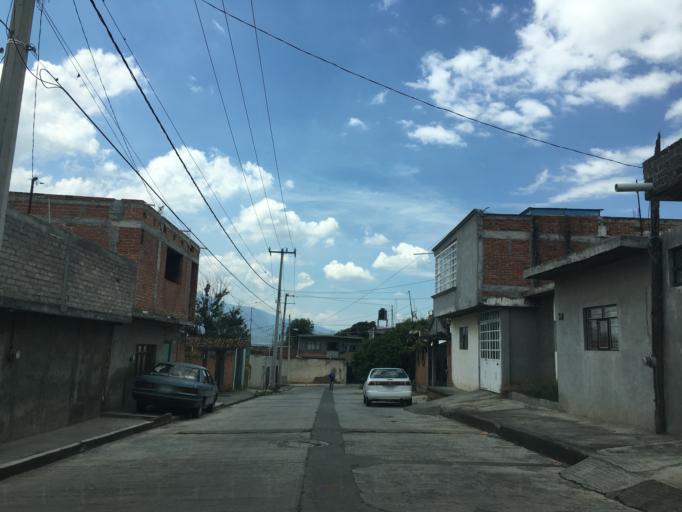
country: MX
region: Michoacan
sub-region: Morelia
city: Morelos
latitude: 19.6484
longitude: -101.2406
